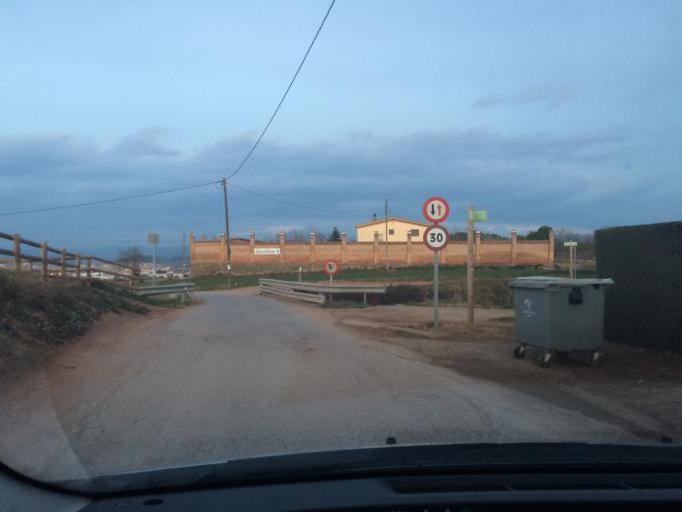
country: ES
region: Catalonia
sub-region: Provincia de Barcelona
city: Sant Fruitos de Bages
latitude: 41.7482
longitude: 1.8474
